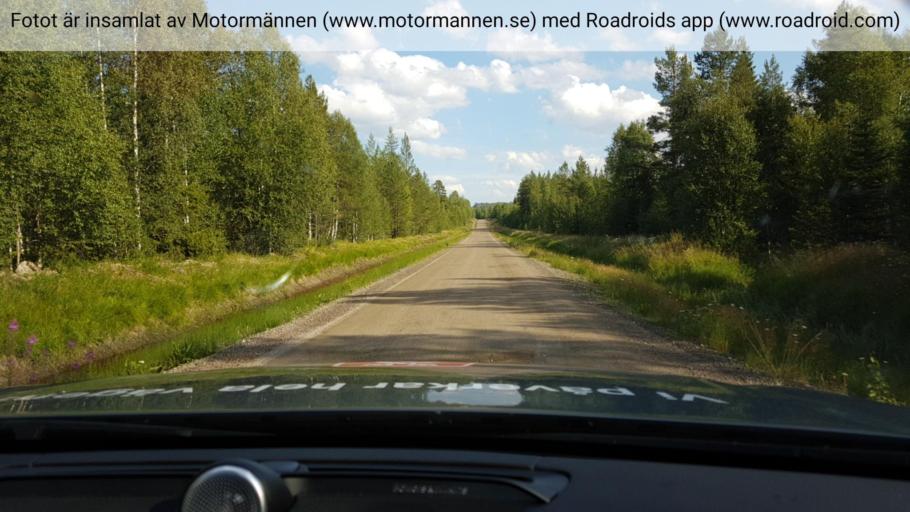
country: SE
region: Jaemtland
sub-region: Stroemsunds Kommun
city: Stroemsund
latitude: 64.0139
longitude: 15.9446
